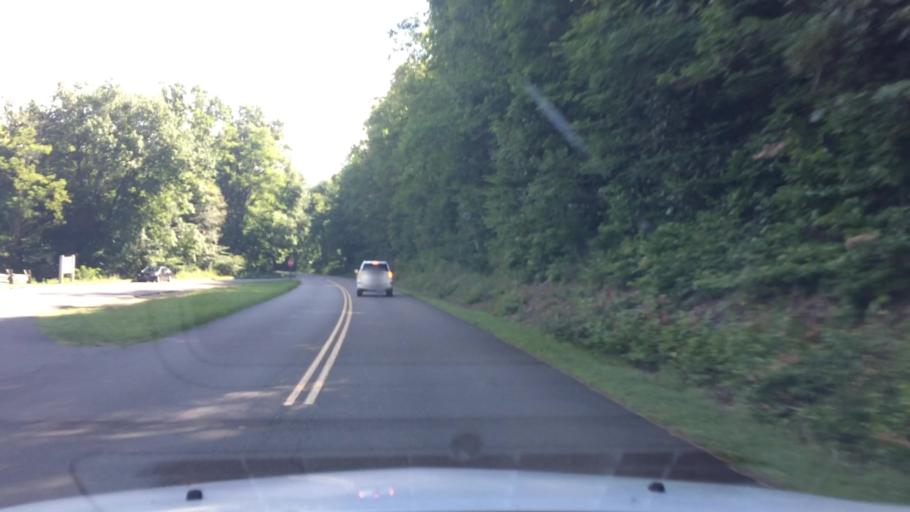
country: US
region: North Carolina
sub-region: Watauga County
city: Blowing Rock
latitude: 36.1427
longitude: -81.7195
